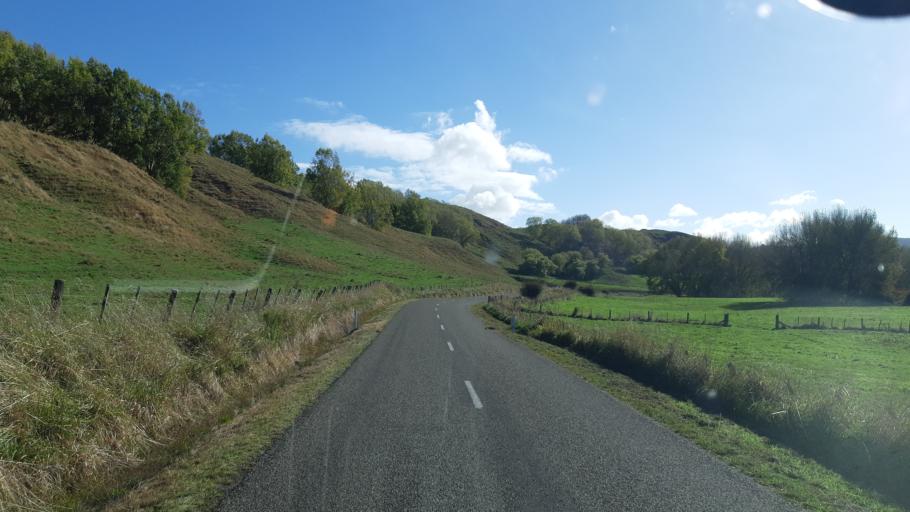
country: NZ
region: Manawatu-Wanganui
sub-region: Wanganui District
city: Wanganui
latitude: -39.8968
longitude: 175.3128
